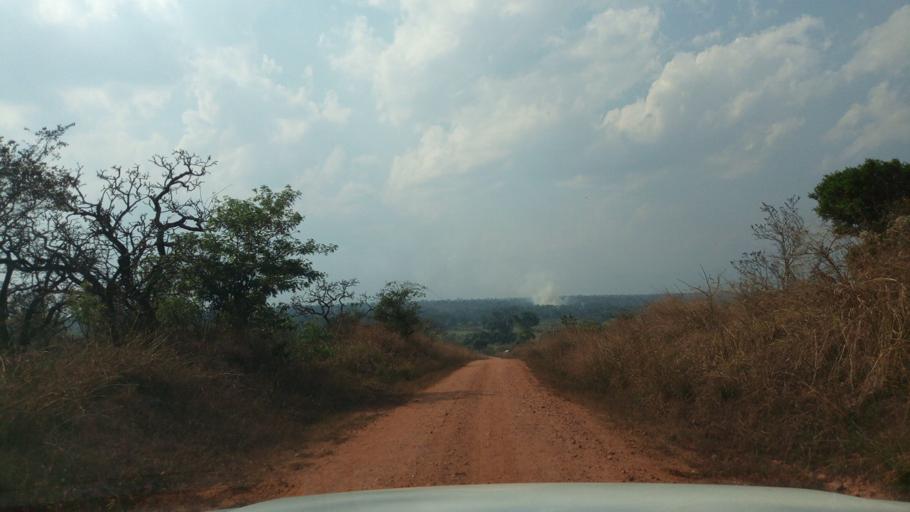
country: CD
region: Katanga
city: Kalemie
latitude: -5.4143
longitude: 28.9339
